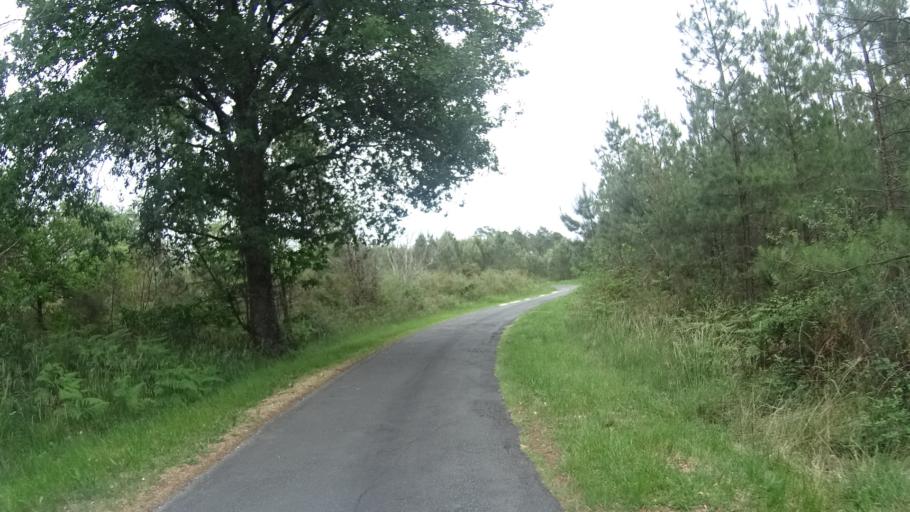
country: FR
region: Aquitaine
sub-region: Departement de la Dordogne
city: Lembras
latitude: 44.9635
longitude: 0.4972
